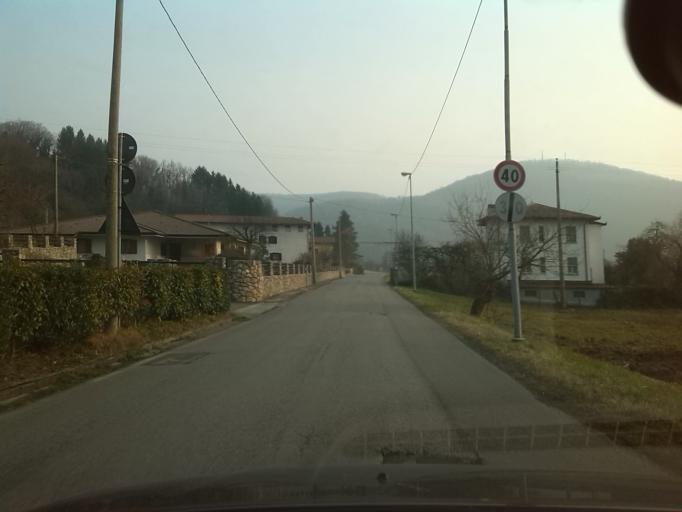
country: IT
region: Friuli Venezia Giulia
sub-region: Provincia di Udine
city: San Pietro al Natisone
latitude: 46.1220
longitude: 13.4852
